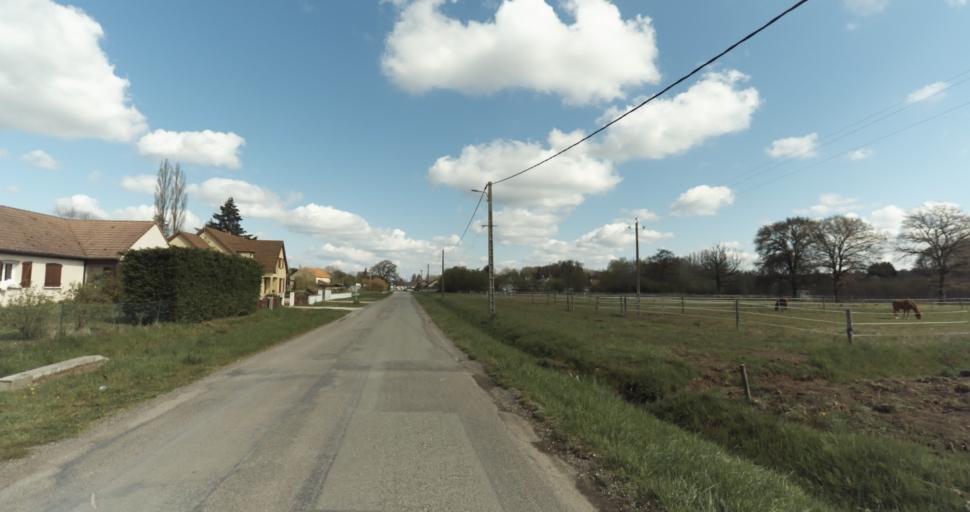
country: FR
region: Bourgogne
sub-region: Departement de la Cote-d'Or
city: Auxonne
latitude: 47.1962
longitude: 5.4246
